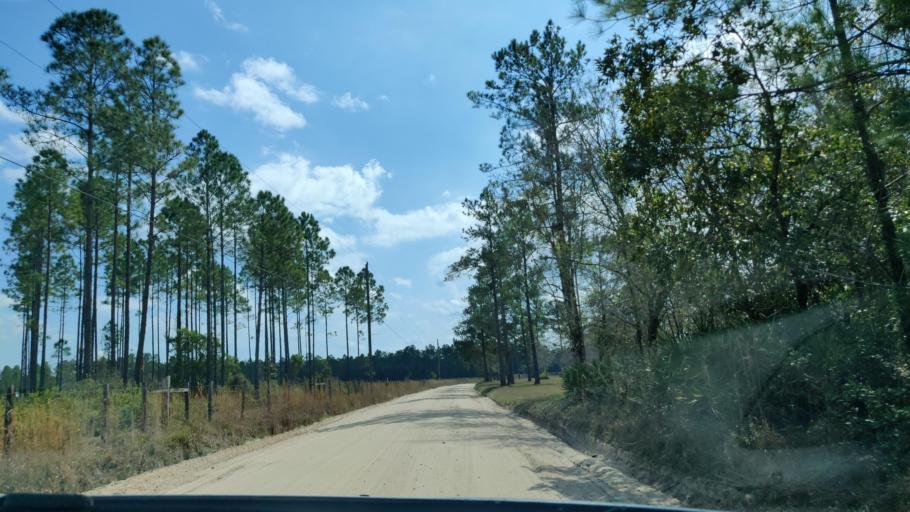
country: US
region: Florida
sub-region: Duval County
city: Baldwin
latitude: 30.1794
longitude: -81.9605
